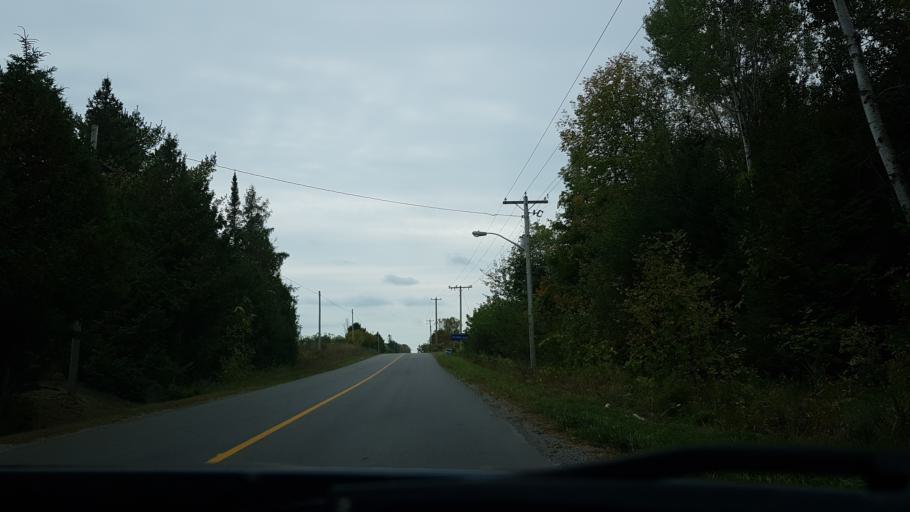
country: CA
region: Ontario
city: Orillia
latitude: 44.6012
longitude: -78.9420
